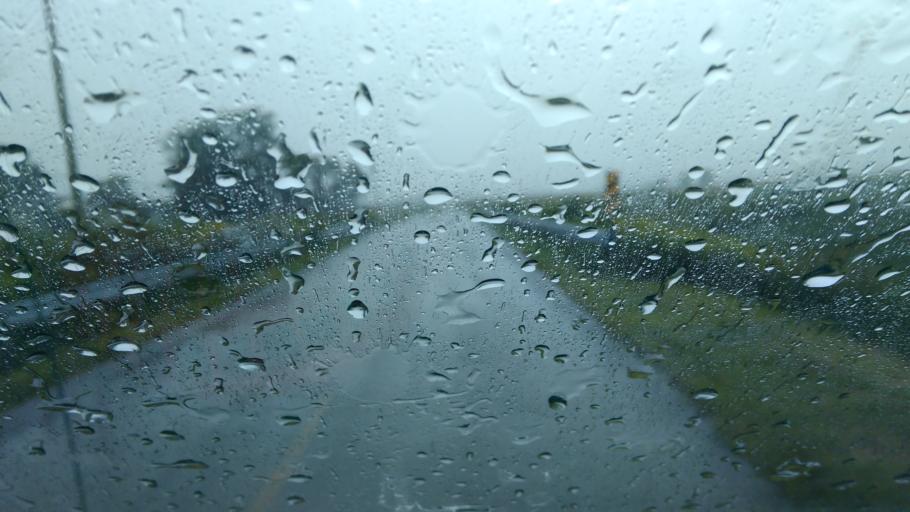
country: US
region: Ohio
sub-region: Hardin County
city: Kenton
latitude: 40.6899
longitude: -83.5379
